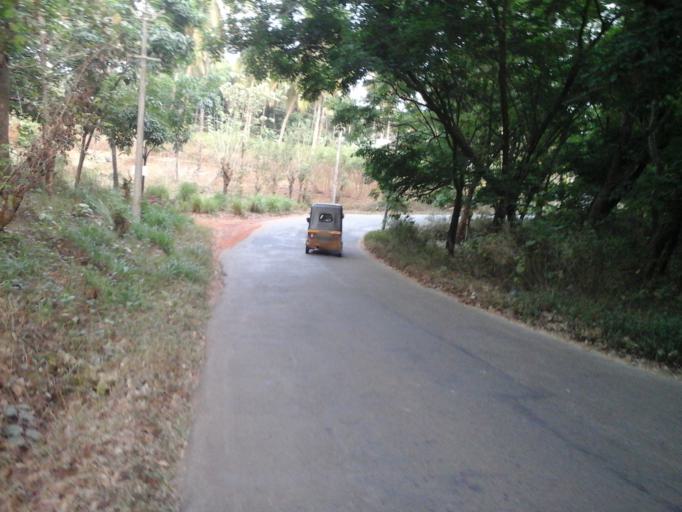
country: IN
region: Kerala
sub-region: Kannur
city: Taliparamba
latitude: 12.1294
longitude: 75.4479
